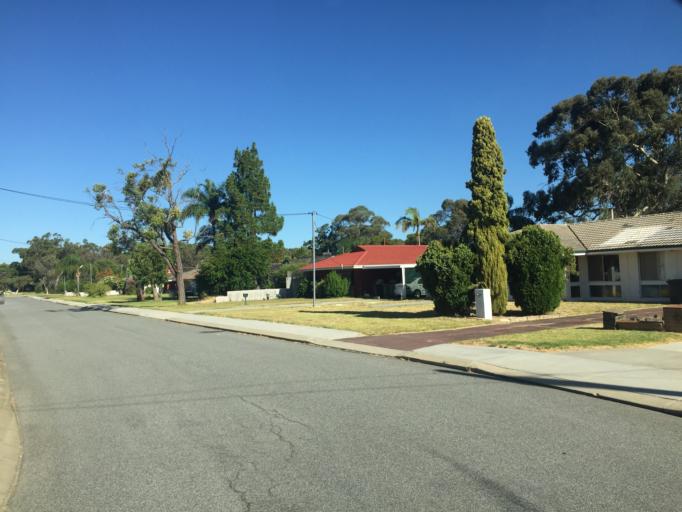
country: AU
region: Western Australia
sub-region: Canning
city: East Cannington
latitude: -32.0141
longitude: 115.9673
